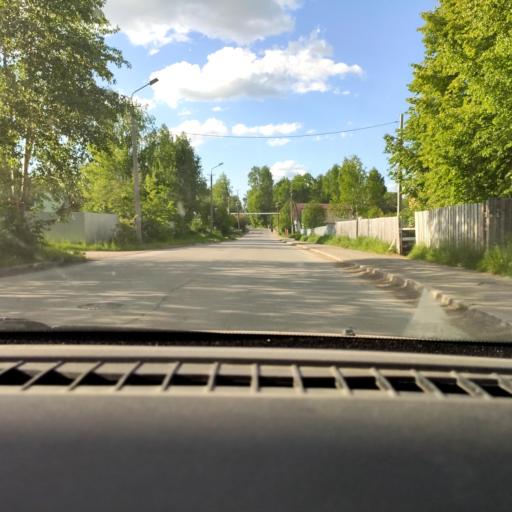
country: RU
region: Perm
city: Polazna
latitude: 58.1468
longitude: 56.4328
